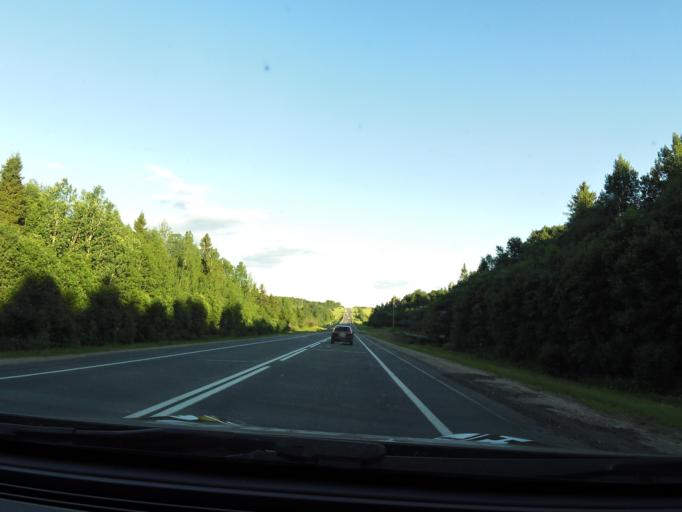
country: RU
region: Vologda
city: Vologda
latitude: 59.1212
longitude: 39.9694
